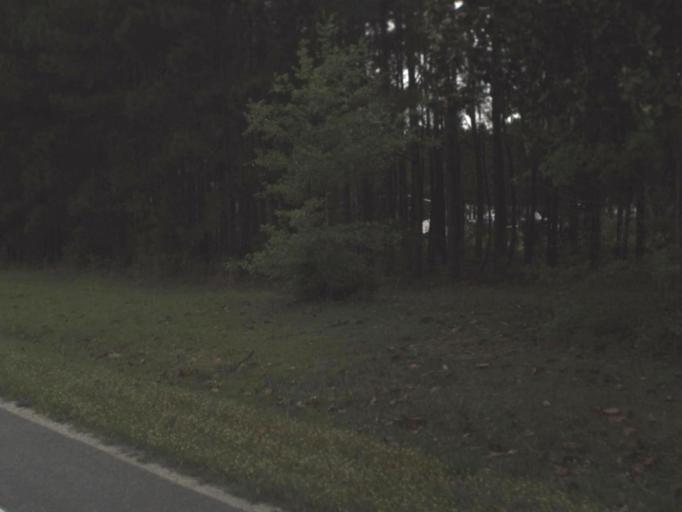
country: US
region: Alabama
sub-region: Escambia County
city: East Brewton
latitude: 30.9263
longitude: -87.0224
